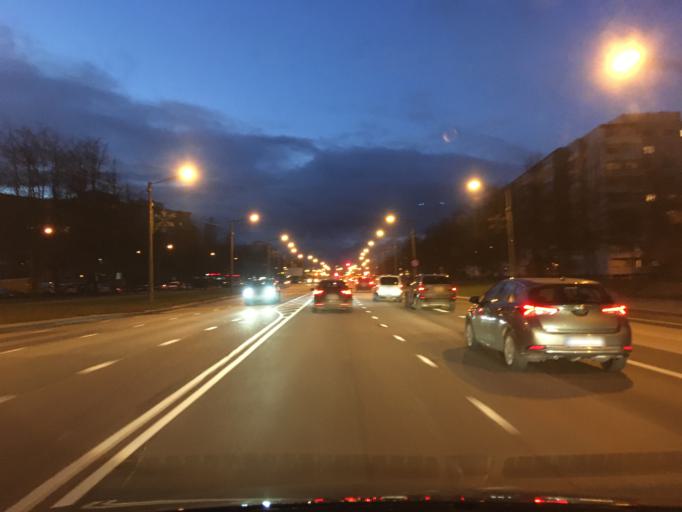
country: EE
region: Harju
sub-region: Tallinna linn
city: Kose
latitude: 59.4347
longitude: 24.8305
